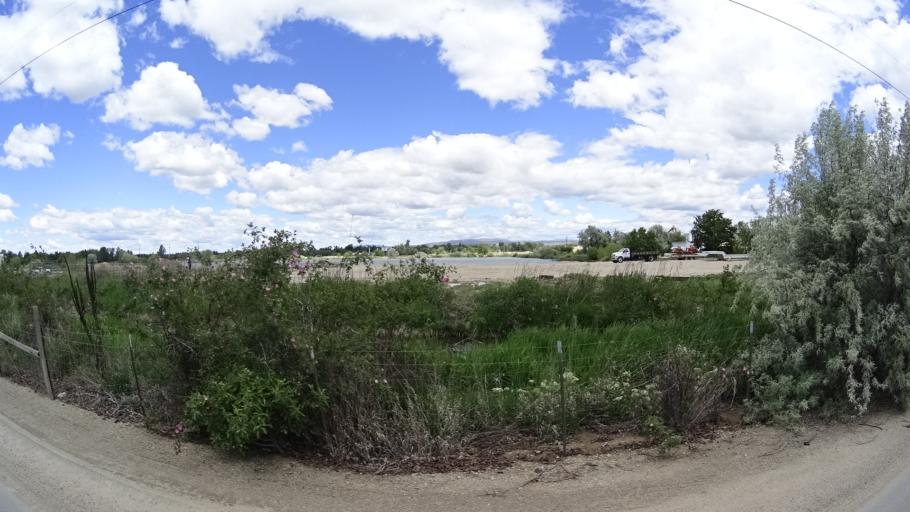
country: US
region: Idaho
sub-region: Ada County
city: Eagle
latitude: 43.6629
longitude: -116.3249
